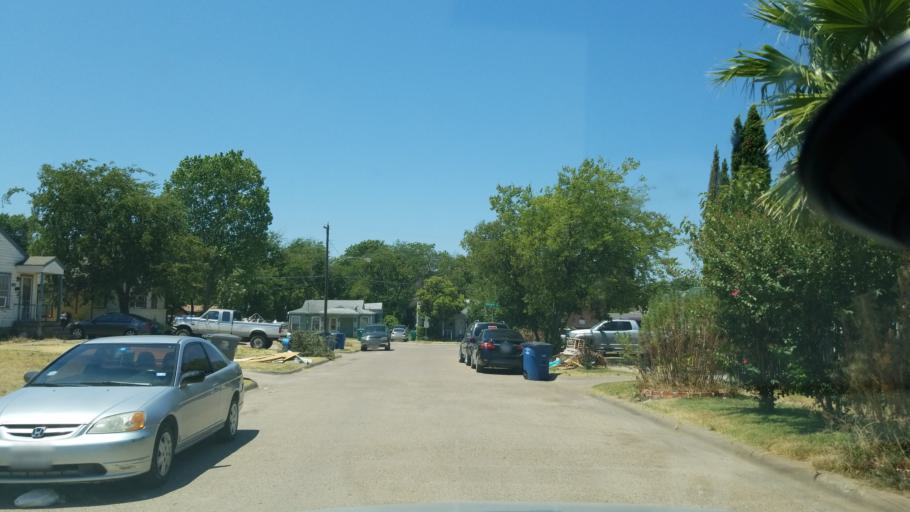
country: US
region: Texas
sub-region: Dallas County
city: Cockrell Hill
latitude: 32.7341
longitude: -96.8870
